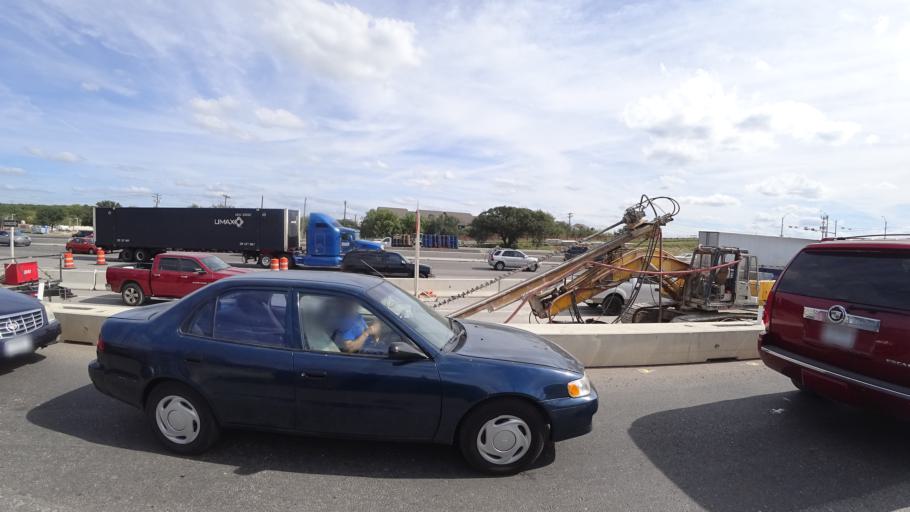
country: US
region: Texas
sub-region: Travis County
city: Onion Creek
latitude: 30.1997
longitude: -97.7636
